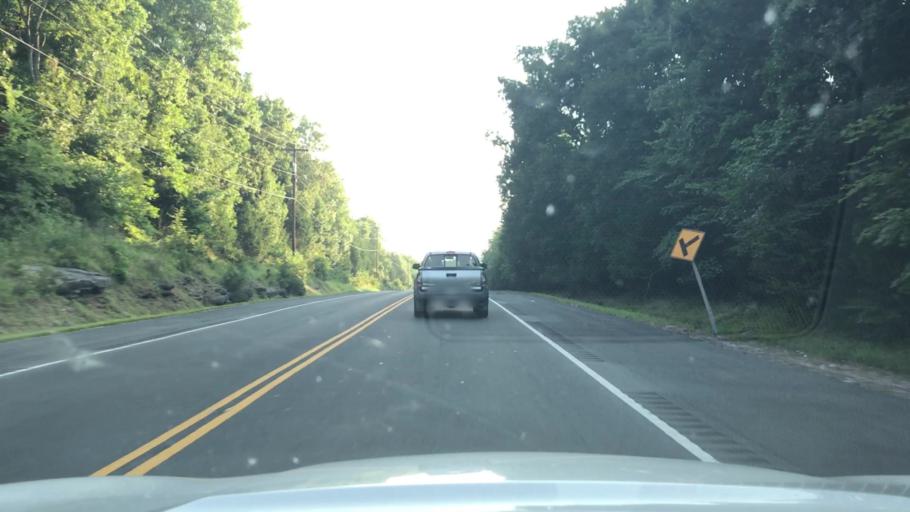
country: US
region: Tennessee
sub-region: Rutherford County
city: La Vergne
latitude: 36.0922
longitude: -86.5591
